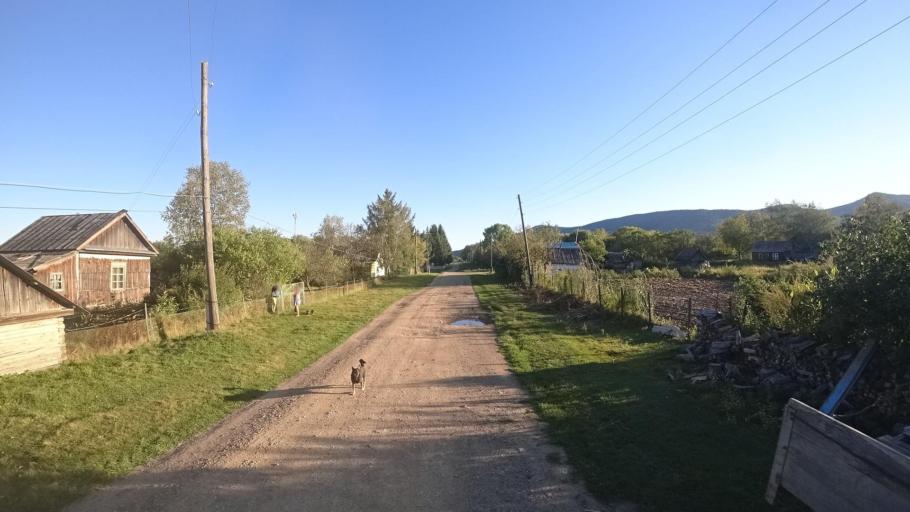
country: RU
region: Primorskiy
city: Kirovskiy
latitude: 44.8327
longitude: 133.5755
